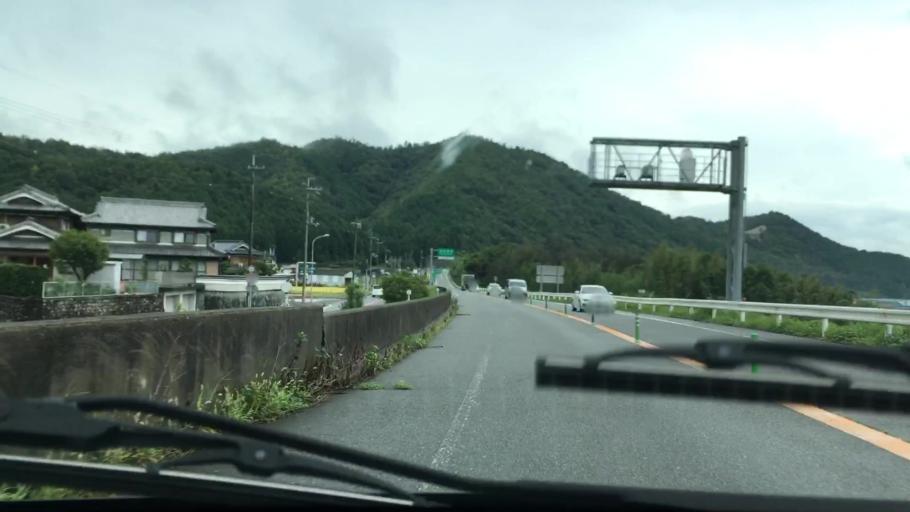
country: JP
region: Hyogo
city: Himeji
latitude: 35.0063
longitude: 134.7648
